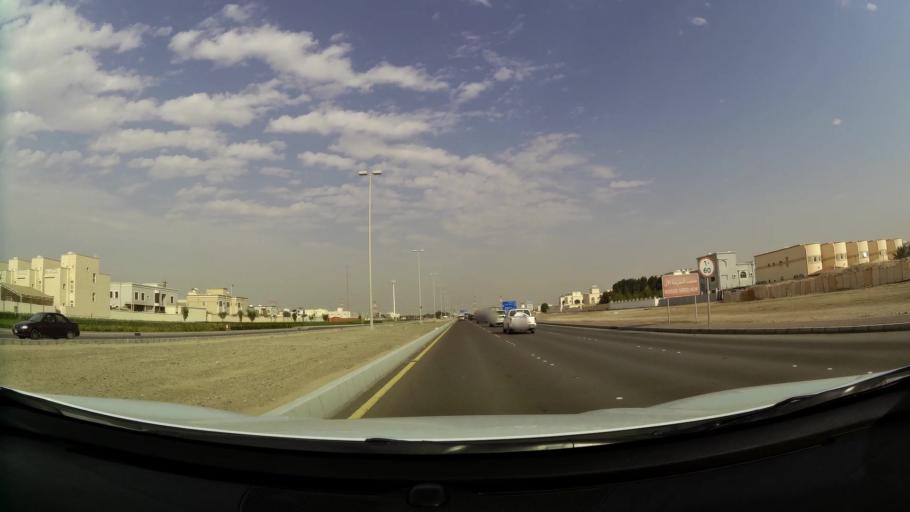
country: AE
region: Abu Dhabi
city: Abu Dhabi
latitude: 24.3259
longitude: 54.5703
